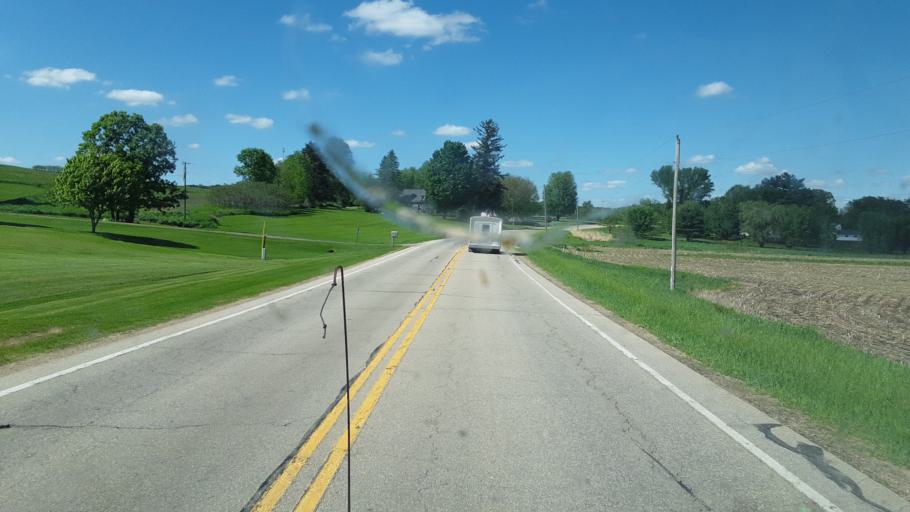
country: US
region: Wisconsin
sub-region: Vernon County
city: Hillsboro
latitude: 43.5156
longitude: -90.2065
